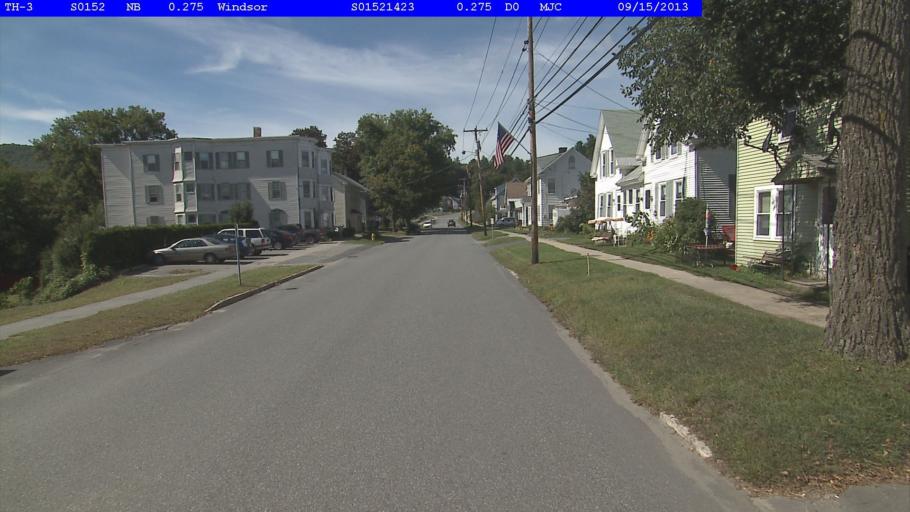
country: US
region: Vermont
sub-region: Windsor County
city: Windsor
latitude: 43.4810
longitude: -72.3917
